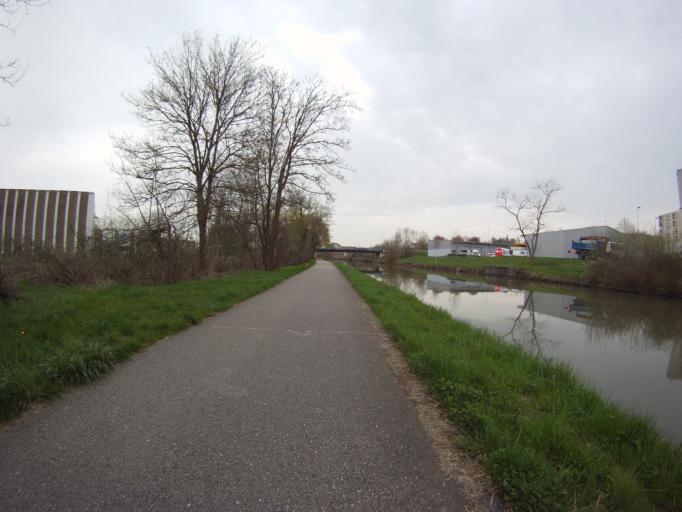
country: FR
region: Lorraine
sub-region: Departement de Meurthe-et-Moselle
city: Jarville-la-Malgrange
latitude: 48.6684
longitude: 6.2121
